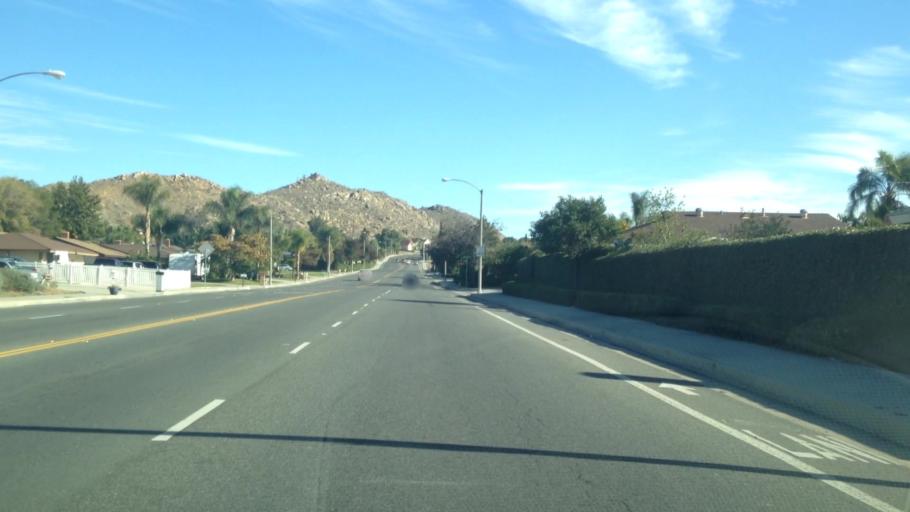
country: US
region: California
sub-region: Riverside County
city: Pedley
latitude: 33.9180
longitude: -117.4730
